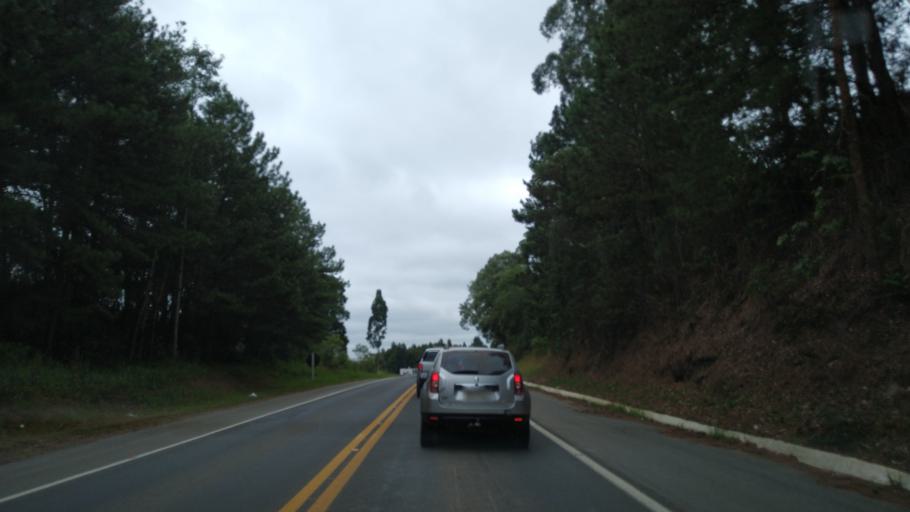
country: BR
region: Santa Catarina
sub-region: Tres Barras
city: Tres Barras
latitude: -26.1815
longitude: -50.2223
